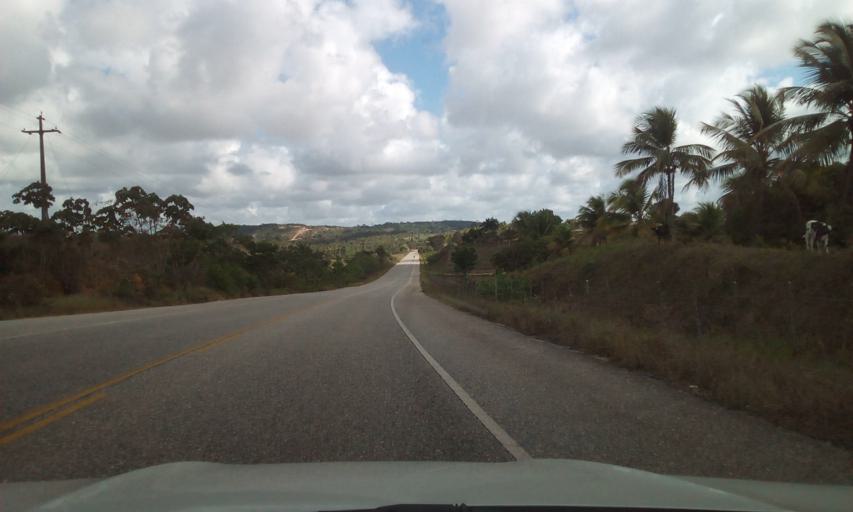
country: BR
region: Sergipe
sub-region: Indiaroba
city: Indiaroba
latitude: -11.4523
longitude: -37.4974
